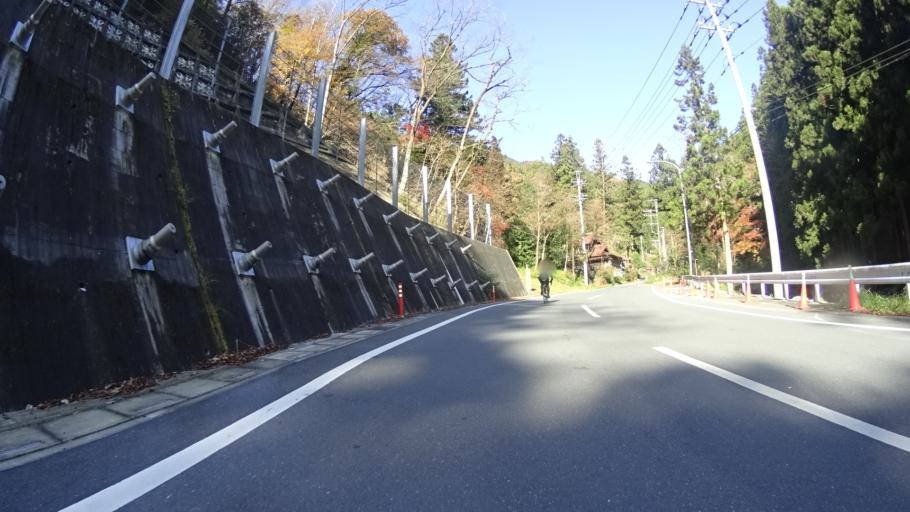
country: JP
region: Saitama
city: Chichibu
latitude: 35.9158
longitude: 139.1506
